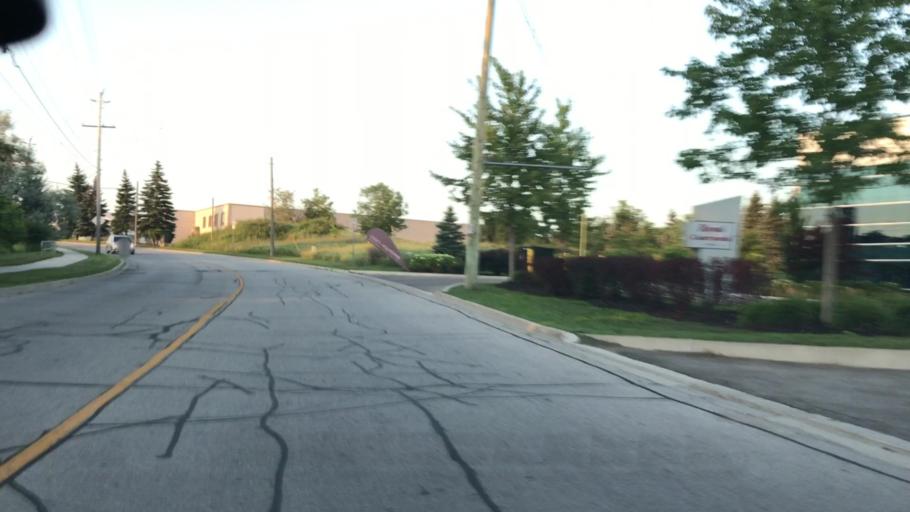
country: CA
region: Ontario
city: Newmarket
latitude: 44.0098
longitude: -79.4617
